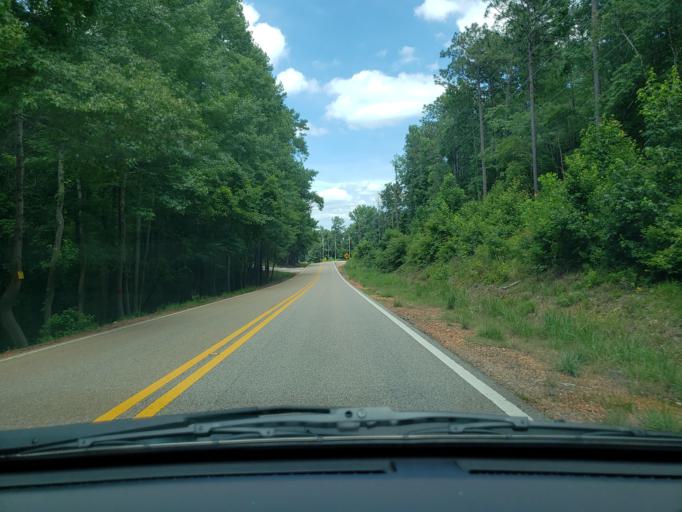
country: US
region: Alabama
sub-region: Elmore County
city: Eclectic
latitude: 32.6721
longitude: -85.9173
